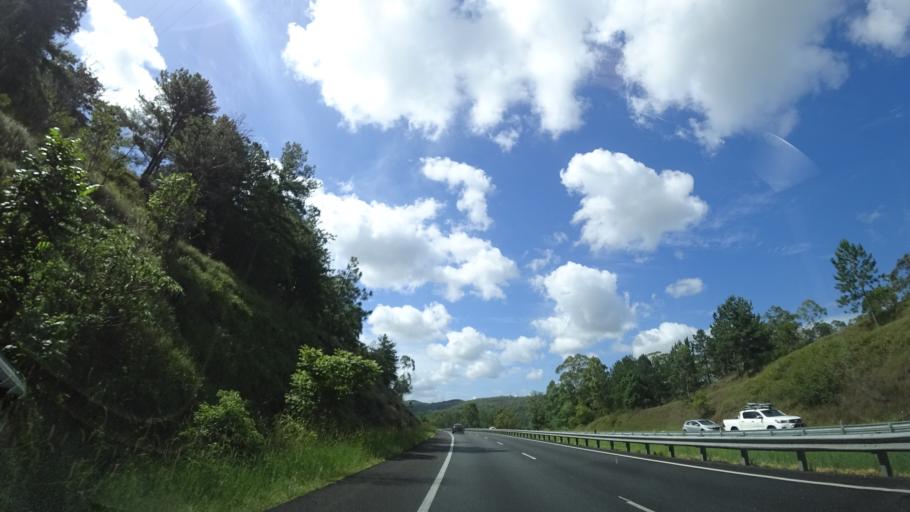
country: AU
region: Queensland
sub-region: Sunshine Coast
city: Twin Waters
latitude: -26.6260
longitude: 152.9880
